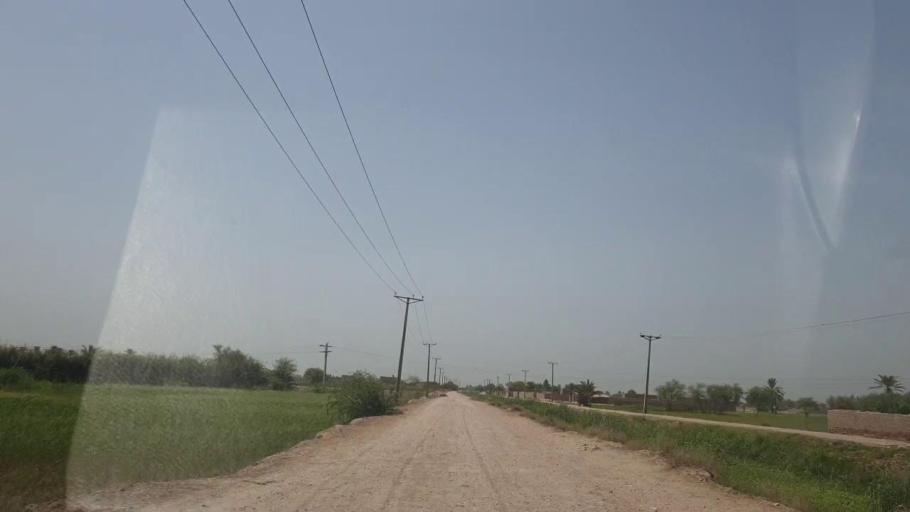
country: PK
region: Sindh
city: Ranipur
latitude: 27.3004
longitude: 68.5453
